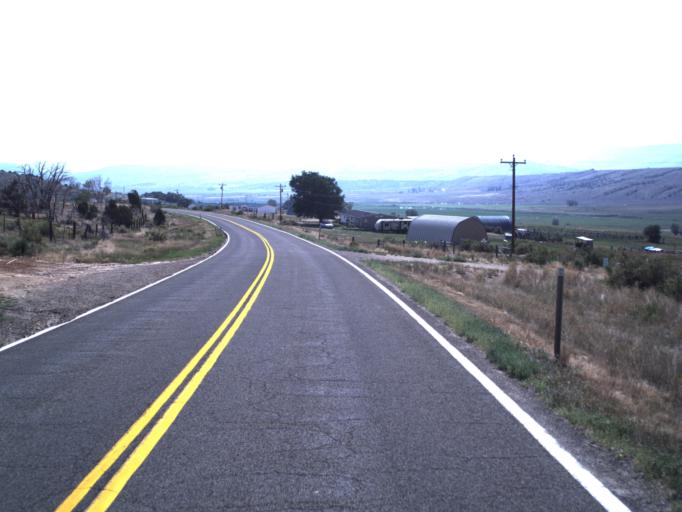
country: US
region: Utah
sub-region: Daggett County
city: Manila
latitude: 40.9774
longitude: -109.7786
